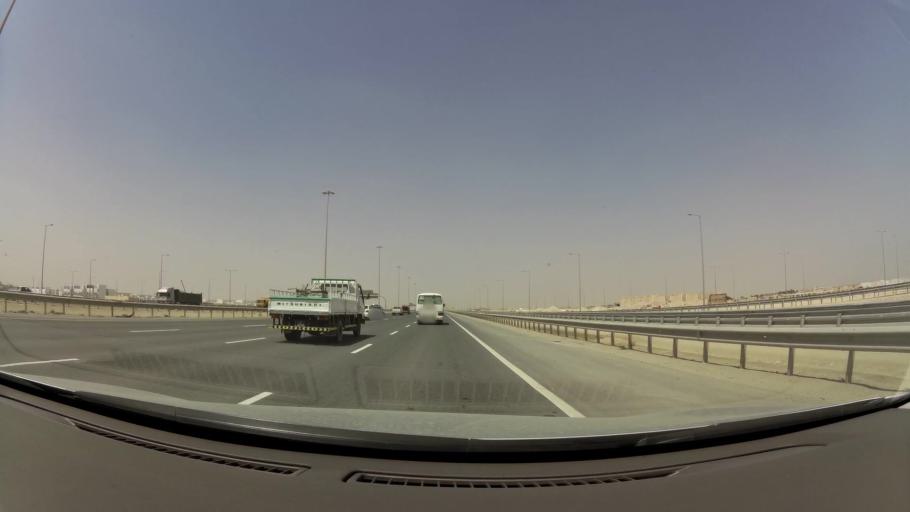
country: QA
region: Baladiyat Umm Salal
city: Umm Salal Muhammad
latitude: 25.4132
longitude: 51.4236
